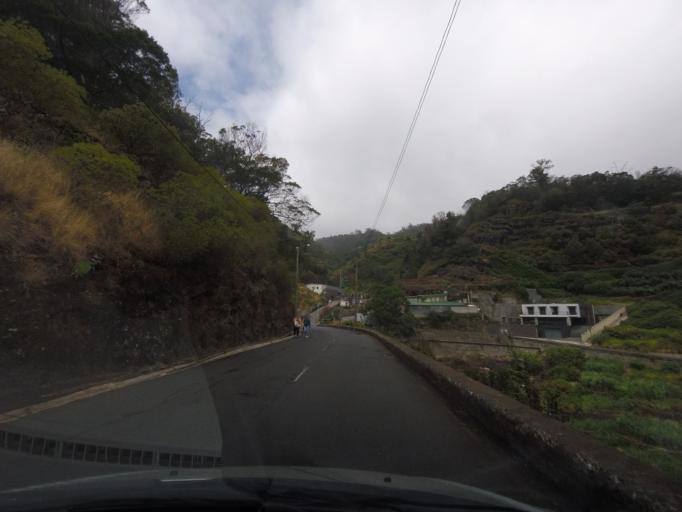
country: PT
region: Madeira
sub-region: Machico
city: Machico
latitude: 32.7061
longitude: -16.7782
